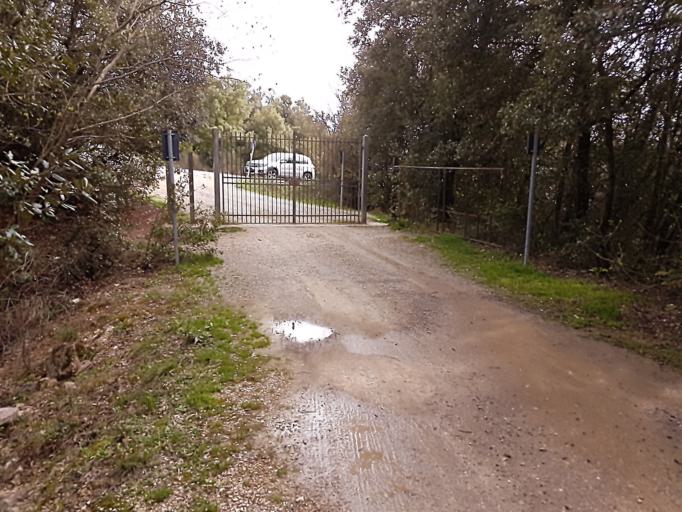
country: IT
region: Umbria
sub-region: Provincia di Perugia
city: Corciano
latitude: 43.1325
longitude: 12.2993
